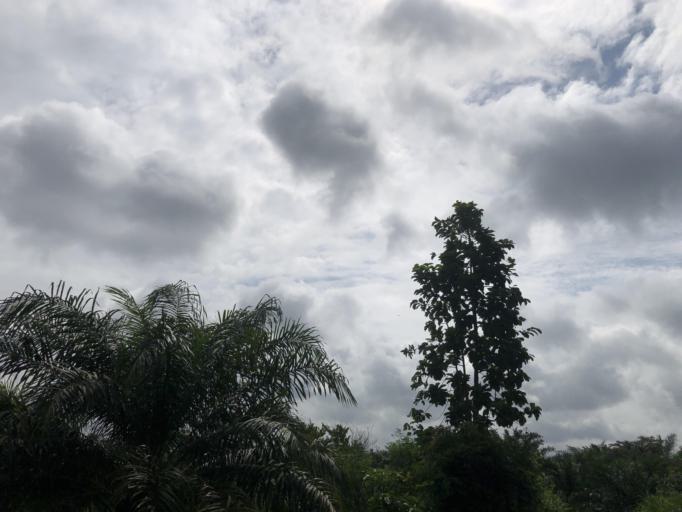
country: SL
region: Eastern Province
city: Kailahun
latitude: 8.2886
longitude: -10.5553
